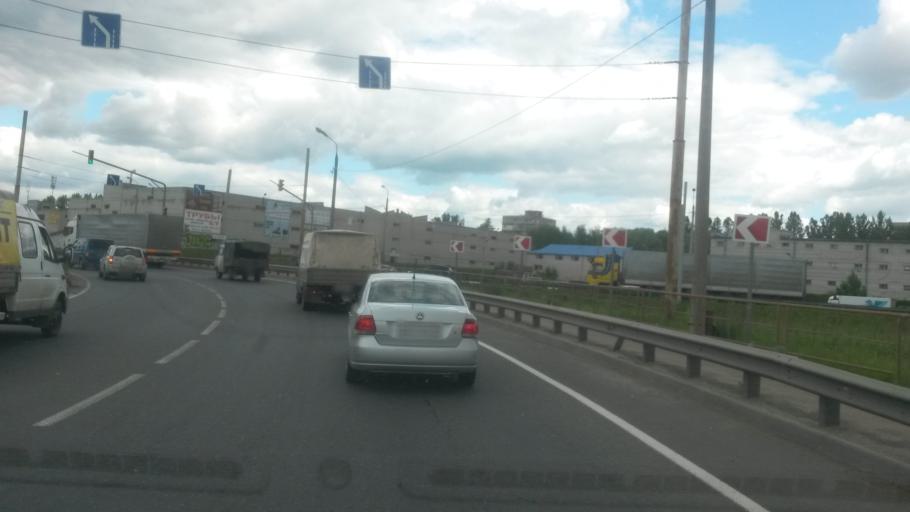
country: RU
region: Jaroslavl
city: Yaroslavl
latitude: 57.6709
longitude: 39.7749
